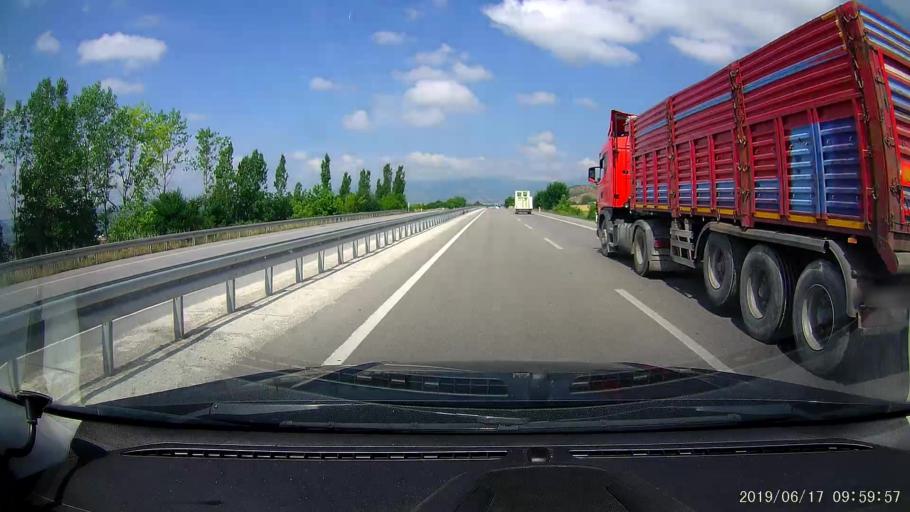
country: TR
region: Amasya
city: Alicik
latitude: 40.8664
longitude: 35.3008
